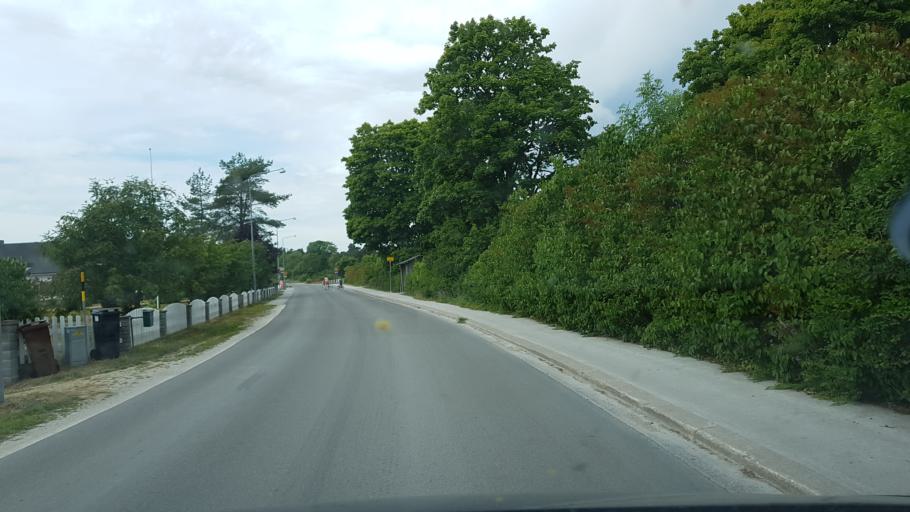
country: SE
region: Gotland
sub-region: Gotland
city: Hemse
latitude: 57.3369
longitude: 18.7015
